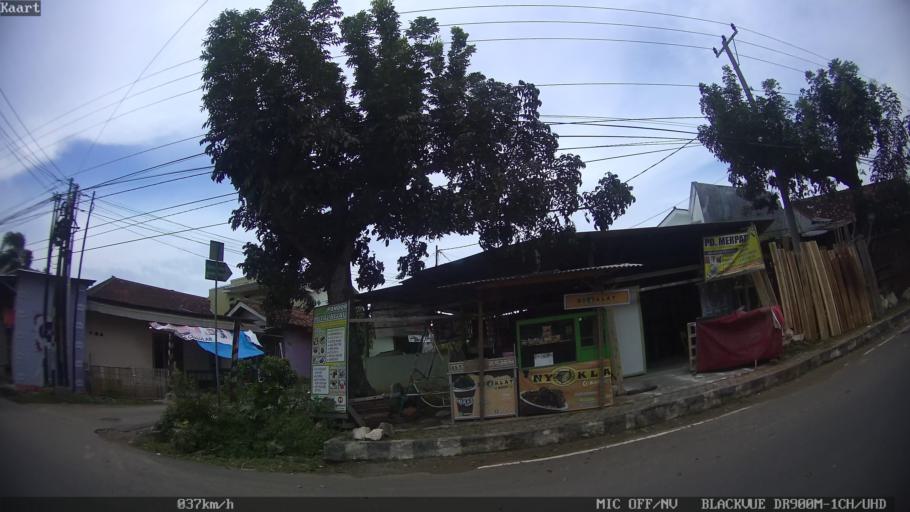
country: ID
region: Lampung
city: Kedaton
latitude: -5.3903
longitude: 105.2183
